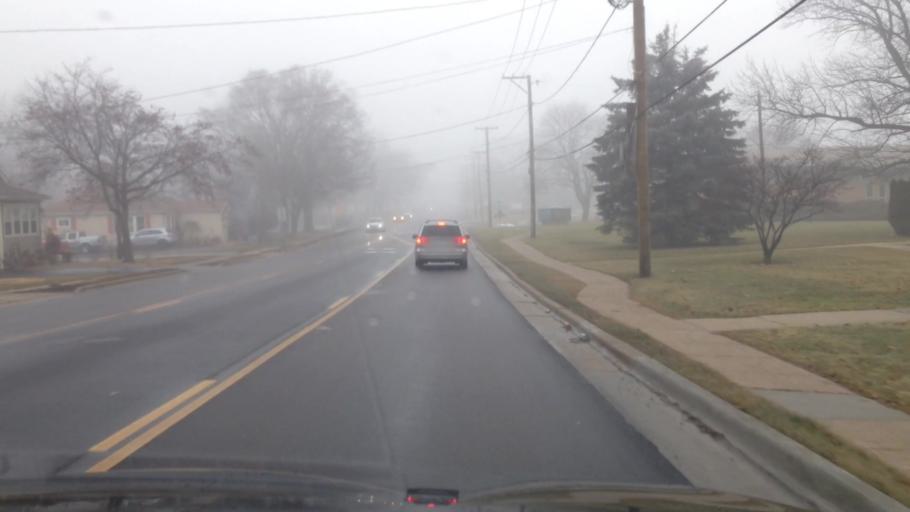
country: US
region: Illinois
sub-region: McHenry County
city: Woodstock
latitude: 42.3240
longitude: -88.4432
